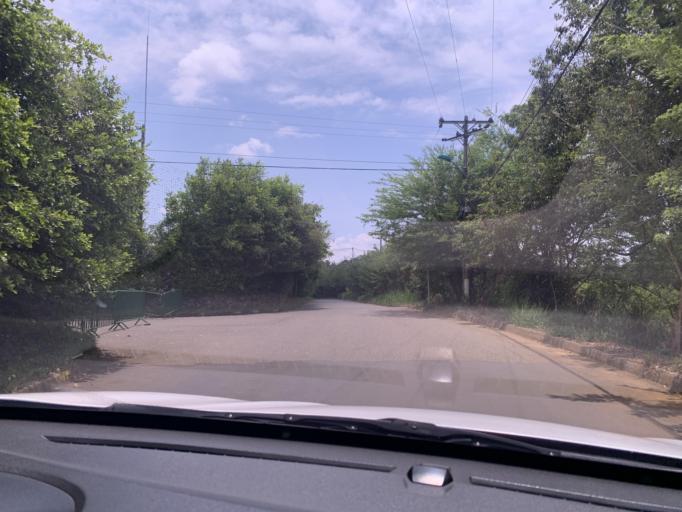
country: CO
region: Valle del Cauca
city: Jamundi
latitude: 3.3374
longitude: -76.5524
